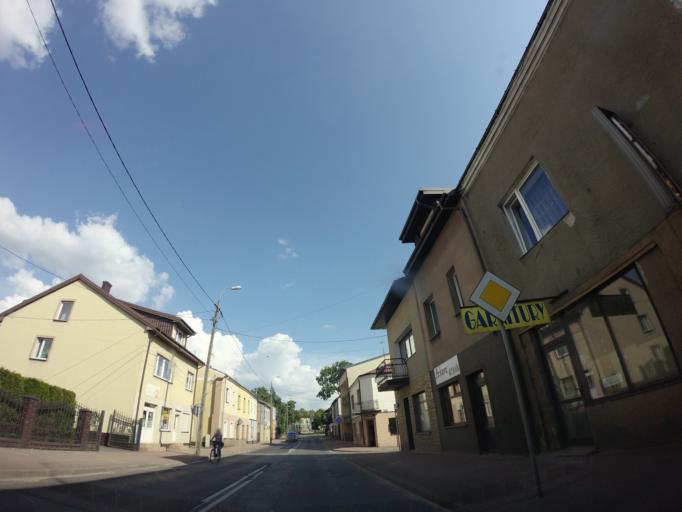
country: PL
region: Masovian Voivodeship
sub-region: Powiat sokolowski
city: Sokolow Podlaski
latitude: 52.4046
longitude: 22.2555
